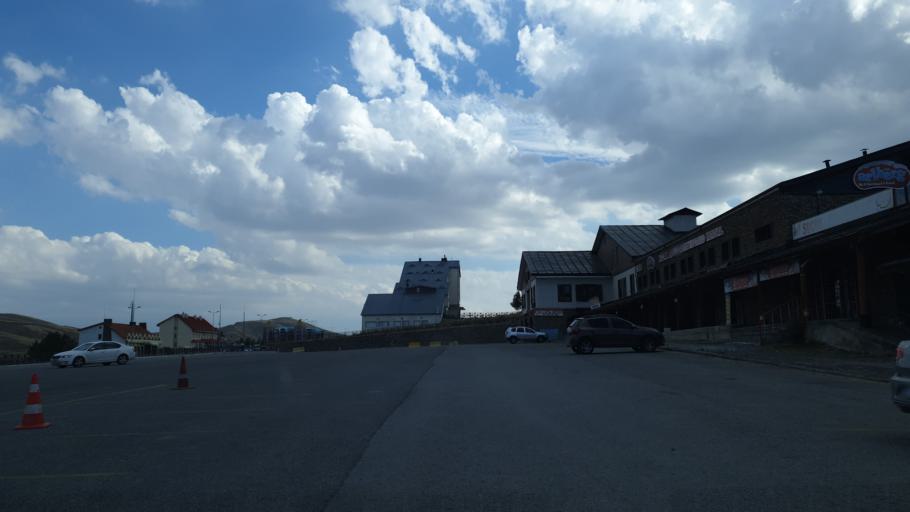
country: TR
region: Kayseri
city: Hacilar
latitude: 38.5395
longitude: 35.5269
